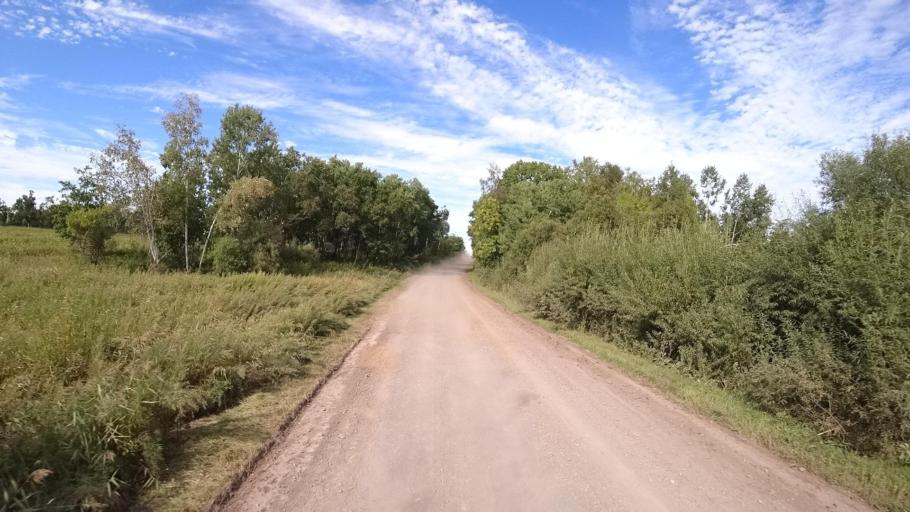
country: RU
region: Primorskiy
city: Dostoyevka
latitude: 44.3763
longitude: 133.5321
